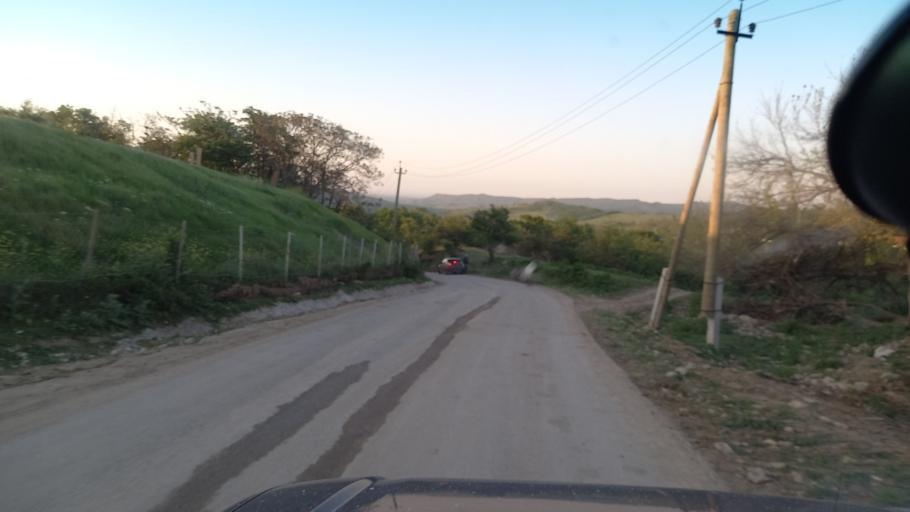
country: RU
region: Dagestan
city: Khuchni
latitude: 42.0241
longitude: 47.9685
